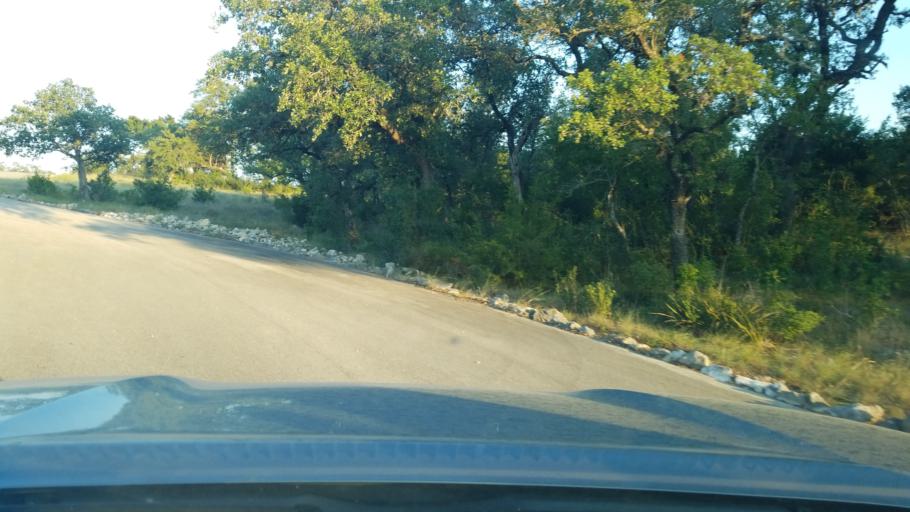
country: US
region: Texas
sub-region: Bexar County
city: Timberwood Park
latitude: 29.6619
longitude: -98.4798
